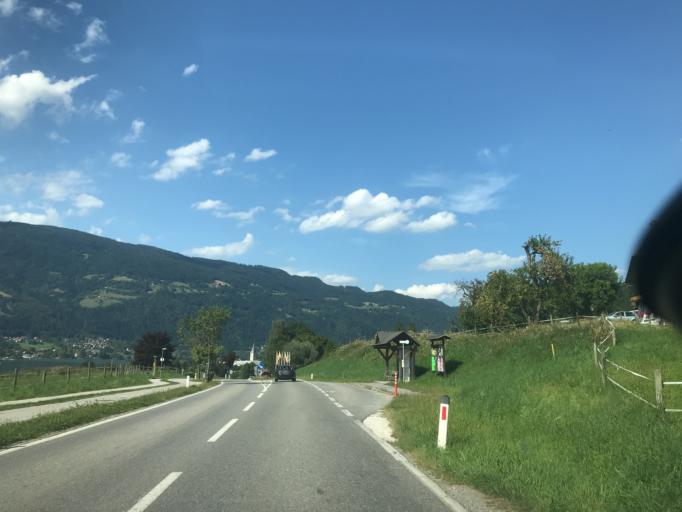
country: AT
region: Carinthia
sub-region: Politischer Bezirk Feldkirchen
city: Ossiach
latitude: 46.6688
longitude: 13.9790
